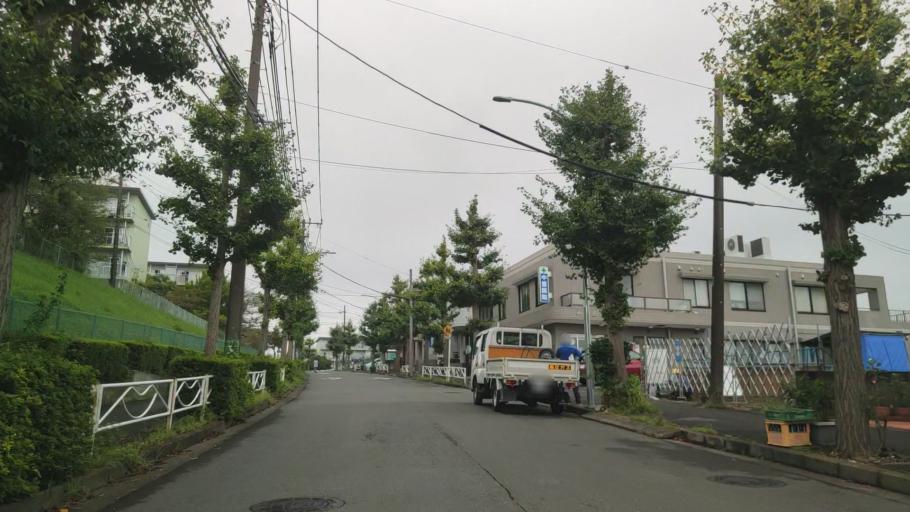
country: JP
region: Kanagawa
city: Zushi
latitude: 35.3651
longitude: 139.6090
